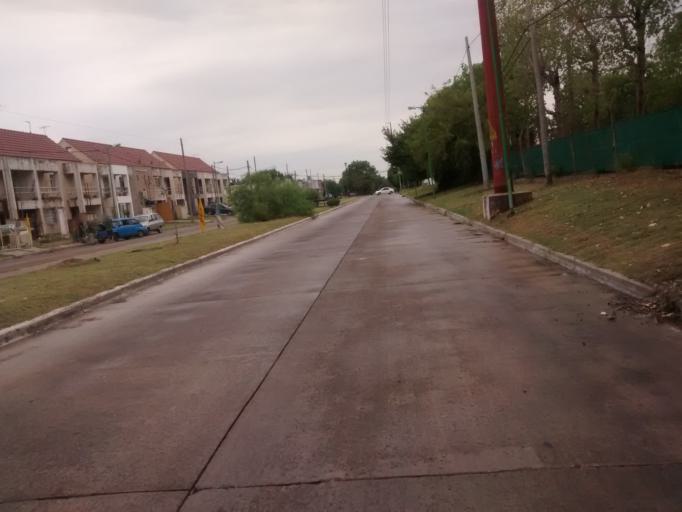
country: AR
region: Buenos Aires
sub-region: Partido de La Plata
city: La Plata
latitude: -34.9058
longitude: -57.9869
